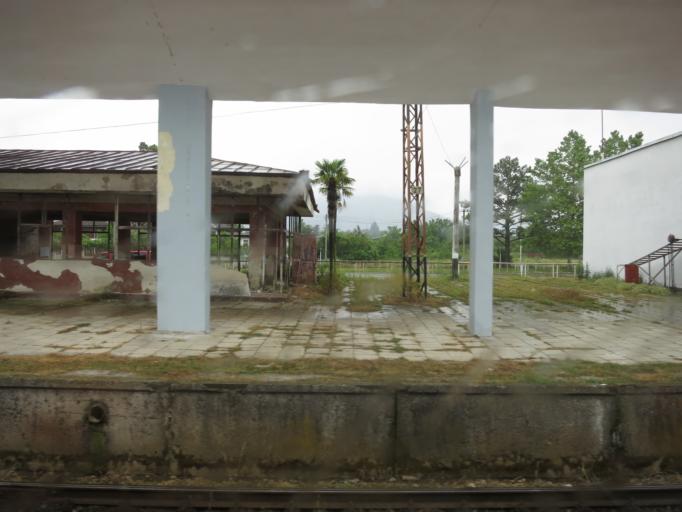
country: GE
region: Guria
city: Lanchkhuti
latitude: 42.0921
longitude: 42.0439
